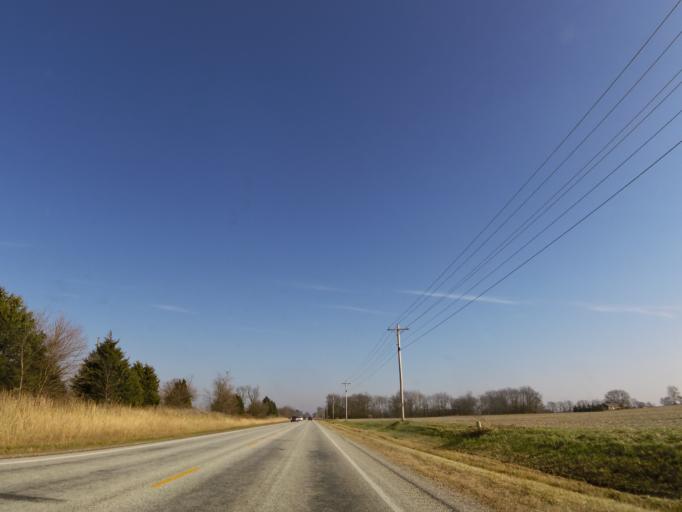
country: US
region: Indiana
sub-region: Shelby County
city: Shelbyville
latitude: 39.5383
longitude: -85.7080
